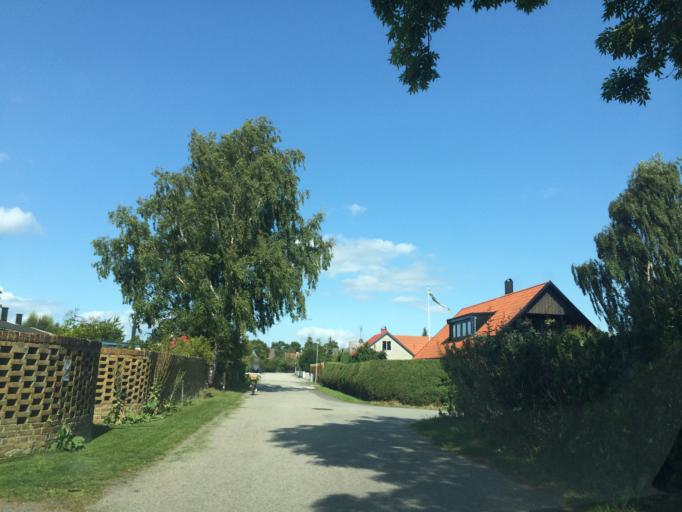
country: SE
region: Skane
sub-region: Vellinge Kommun
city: Skanor med Falsterbo
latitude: 55.3962
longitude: 12.8389
